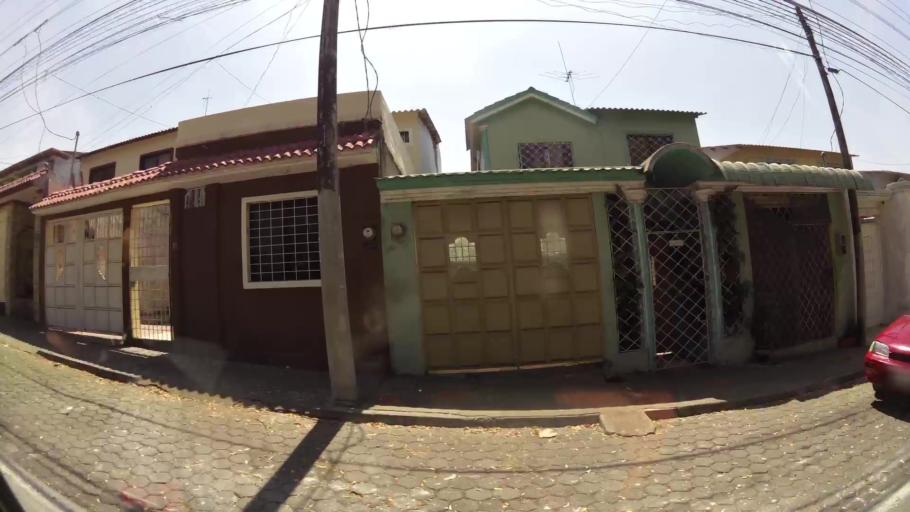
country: EC
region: Guayas
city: Eloy Alfaro
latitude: -2.1111
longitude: -79.9064
